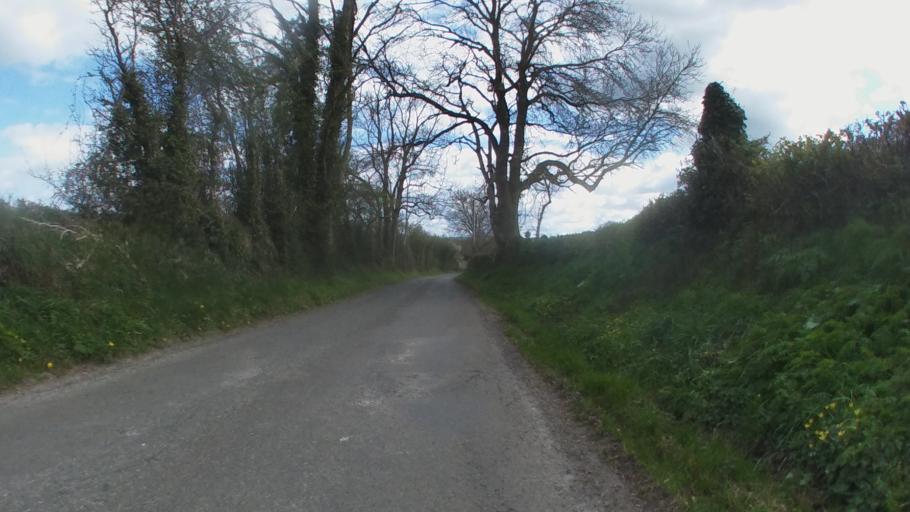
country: IE
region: Leinster
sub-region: Kilkenny
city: Kilkenny
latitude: 52.7020
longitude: -7.2048
